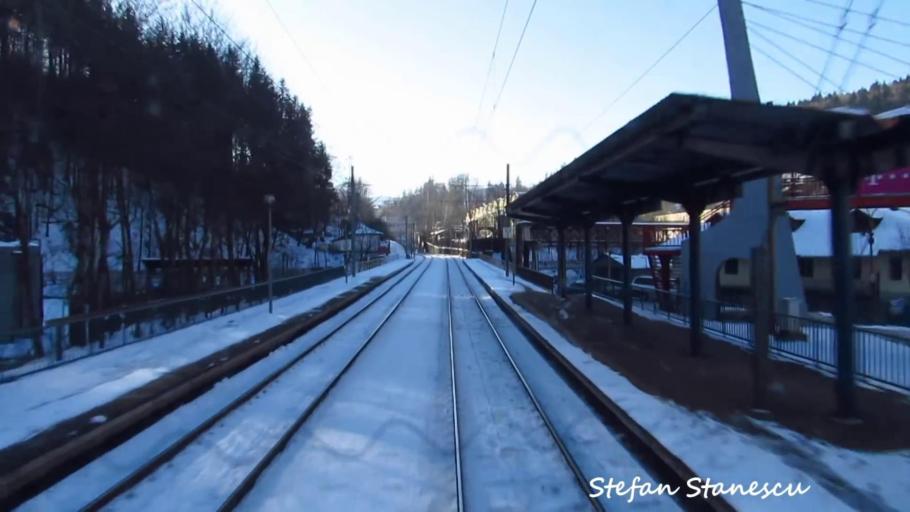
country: RO
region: Prahova
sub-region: Oras Sinaia
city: Sinaia
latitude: 45.3398
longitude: 25.5522
